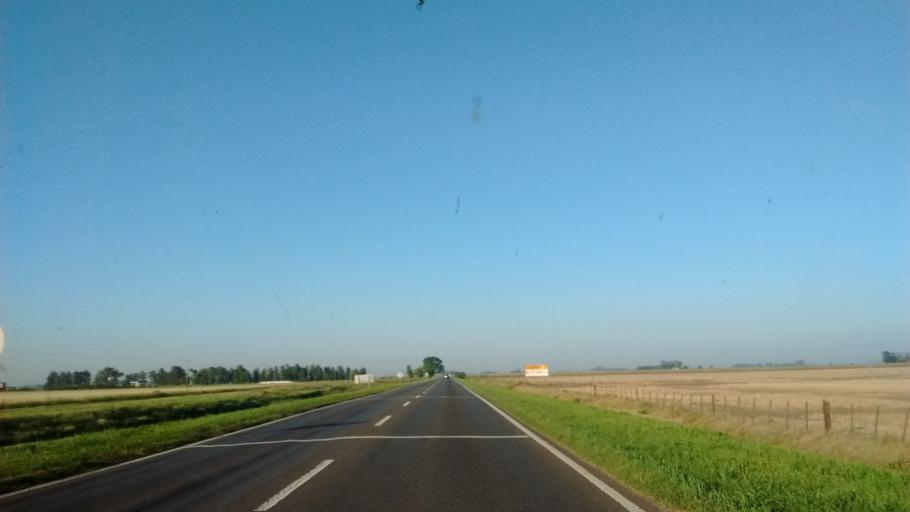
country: AR
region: Santa Fe
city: Firmat
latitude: -33.5497
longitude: -61.6708
